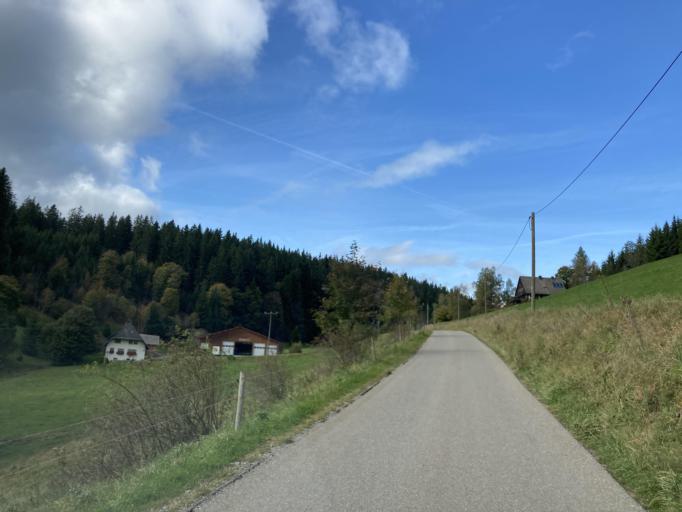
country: DE
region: Baden-Wuerttemberg
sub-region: Freiburg Region
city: Vohrenbach
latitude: 48.0647
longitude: 8.2846
